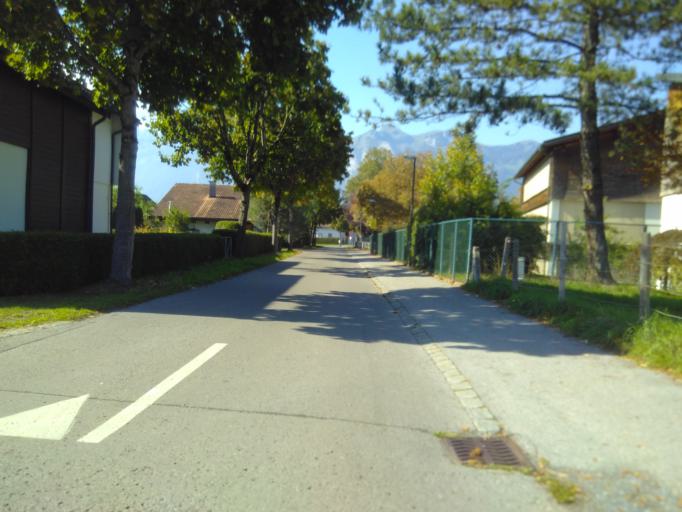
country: AT
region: Vorarlberg
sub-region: Politischer Bezirk Feldkirch
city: Nofels
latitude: 47.2579
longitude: 9.5734
